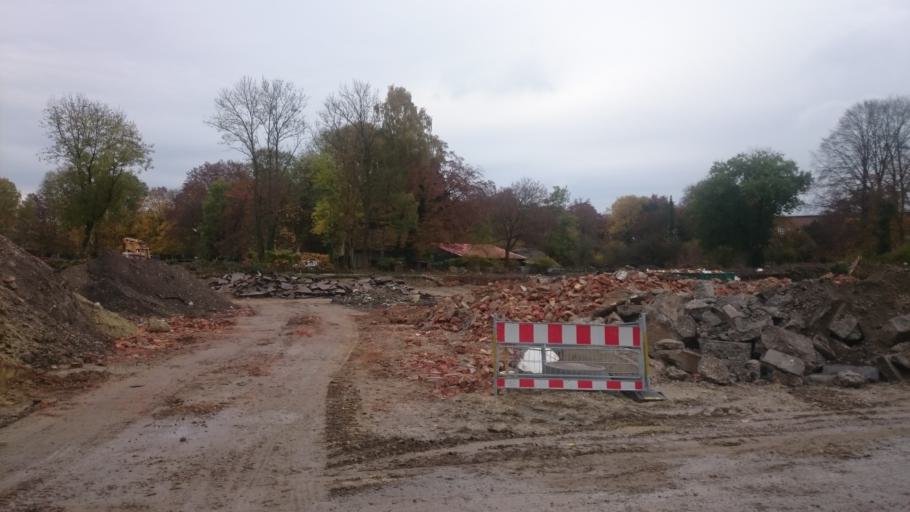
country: DE
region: Bavaria
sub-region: Swabia
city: Augsburg
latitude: 48.3652
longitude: 10.9154
